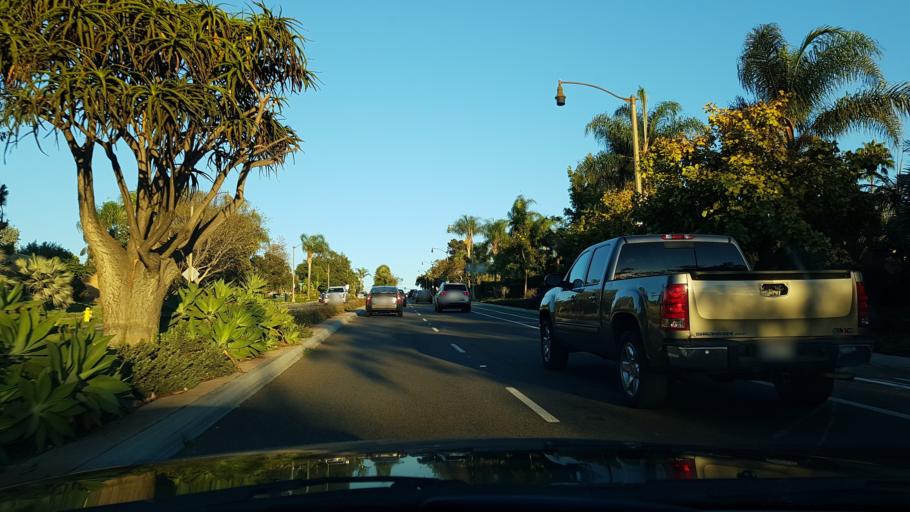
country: US
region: California
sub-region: San Diego County
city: Encinitas
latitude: 33.0652
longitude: -117.2845
